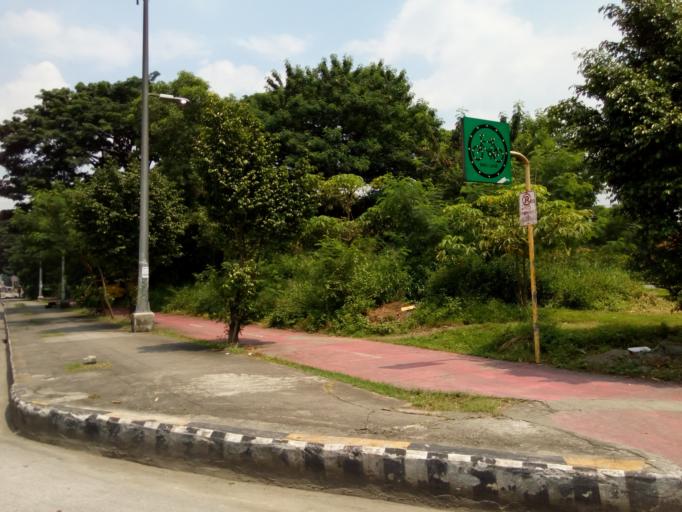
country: PH
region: Metro Manila
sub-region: Quezon City
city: Quezon City
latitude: 14.6552
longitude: 121.0560
